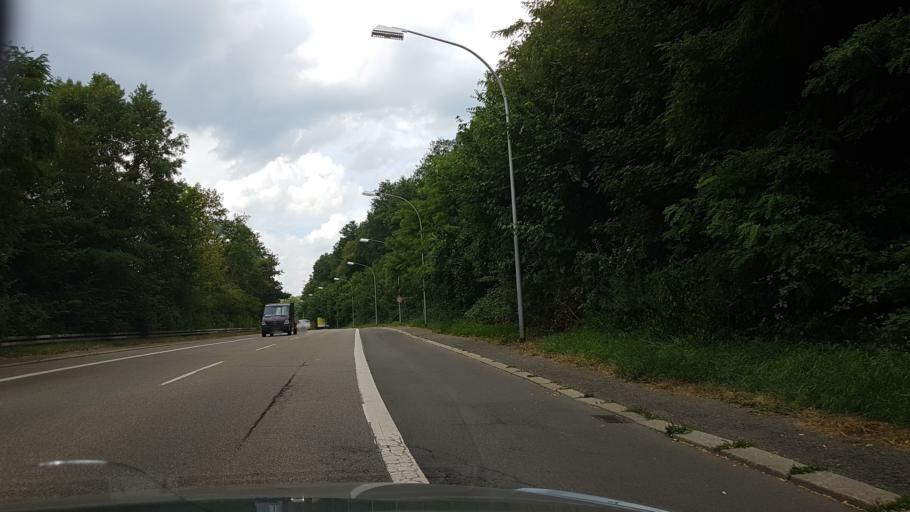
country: DE
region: Saarland
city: Saarbrucken
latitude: 49.2549
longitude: 7.0032
